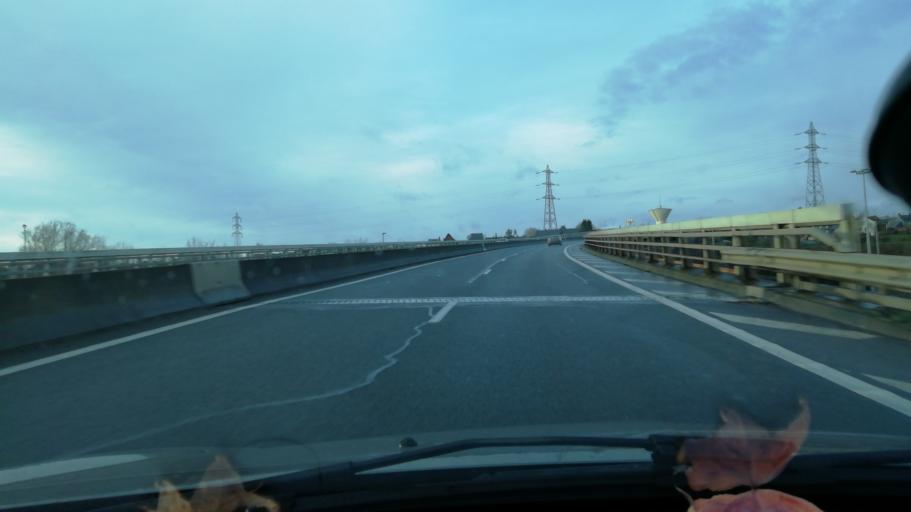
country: FR
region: Nord-Pas-de-Calais
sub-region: Departement du Nord
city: Hautmont
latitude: 50.2620
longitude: 3.9274
